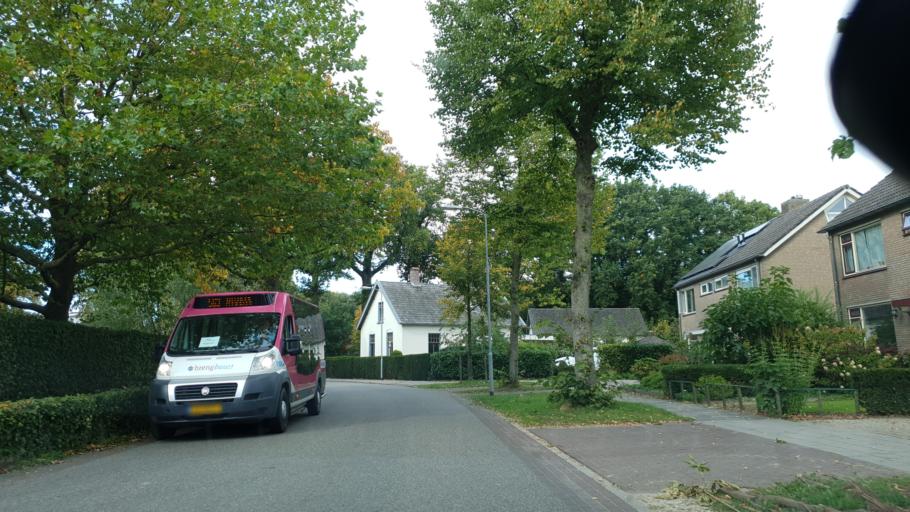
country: NL
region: Gelderland
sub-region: Gemeente Wijchen
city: Bergharen
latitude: 51.8510
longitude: 5.6630
